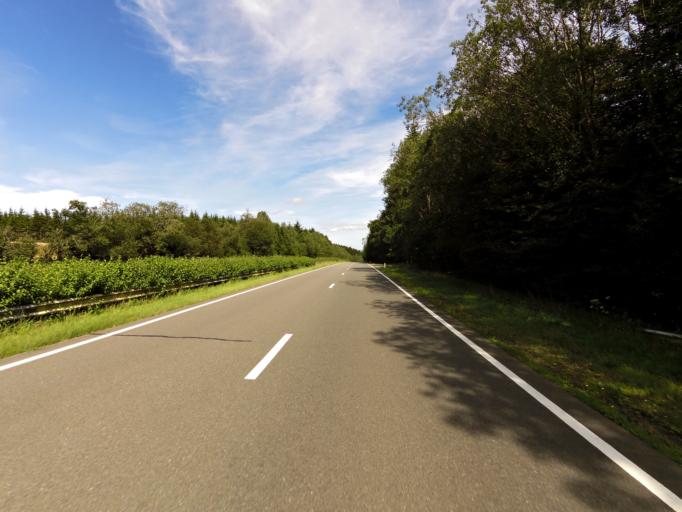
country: BE
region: Wallonia
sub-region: Province du Luxembourg
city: Tenneville
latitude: 50.0971
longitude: 5.4595
